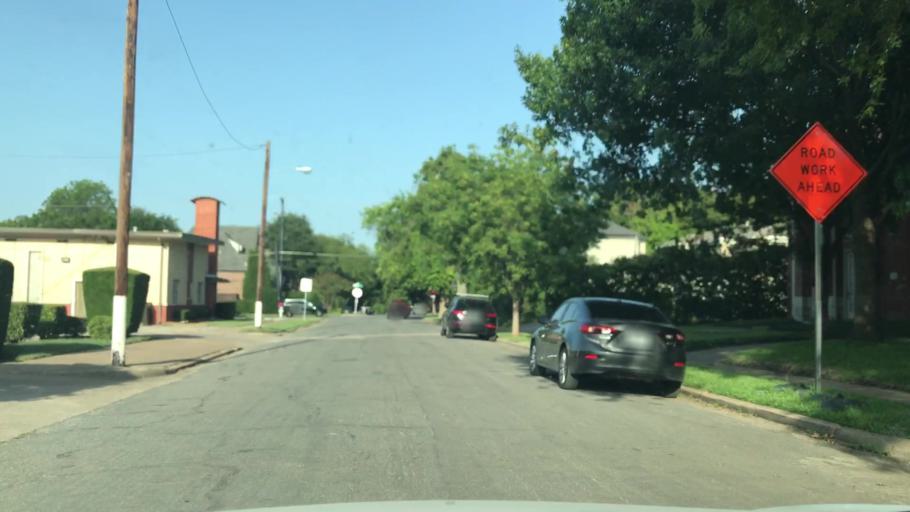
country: US
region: Texas
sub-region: Dallas County
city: Highland Park
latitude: 32.8220
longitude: -96.7539
